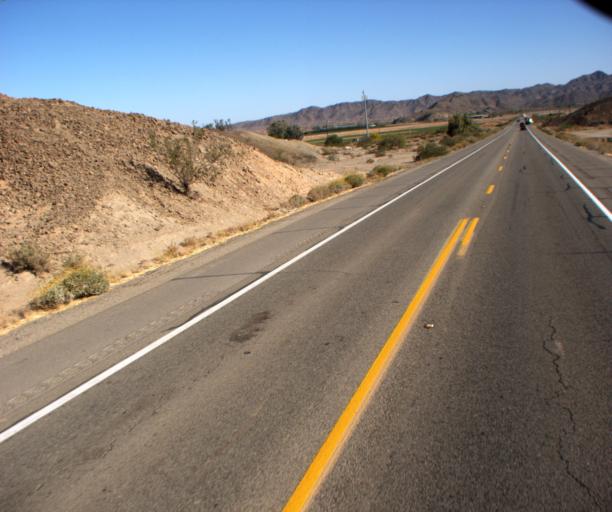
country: US
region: Arizona
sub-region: Yuma County
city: Fortuna Foothills
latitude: 32.7444
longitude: -114.4242
